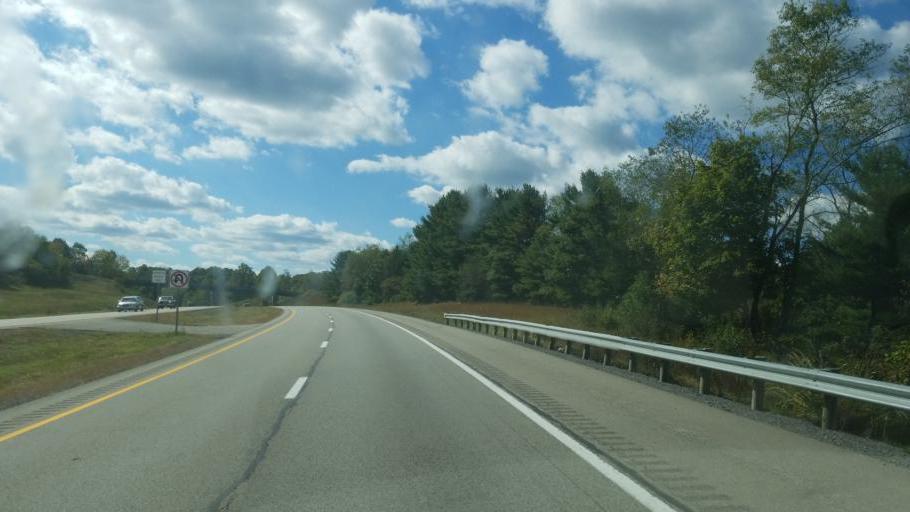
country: US
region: Pennsylvania
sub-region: Fayette County
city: Fairchance
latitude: 39.6633
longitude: -79.6709
